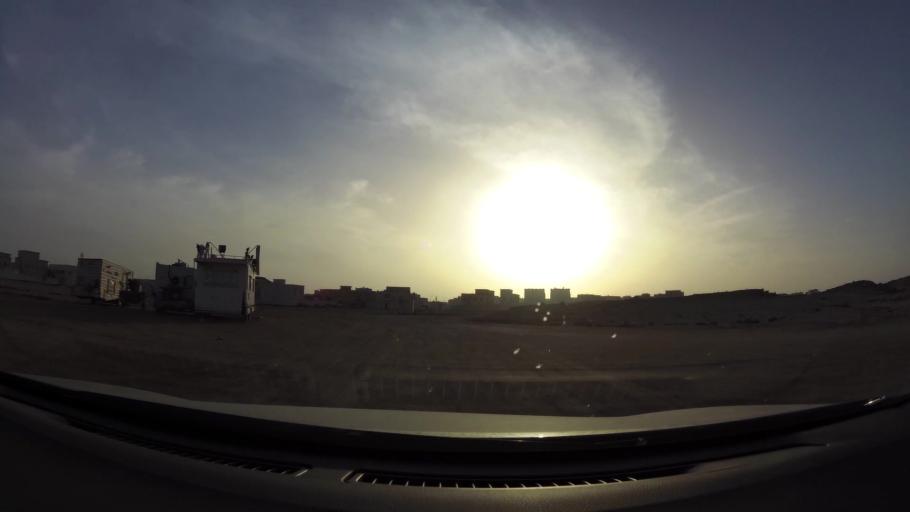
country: QA
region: Al Wakrah
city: Al Wakrah
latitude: 25.1455
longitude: 51.6160
